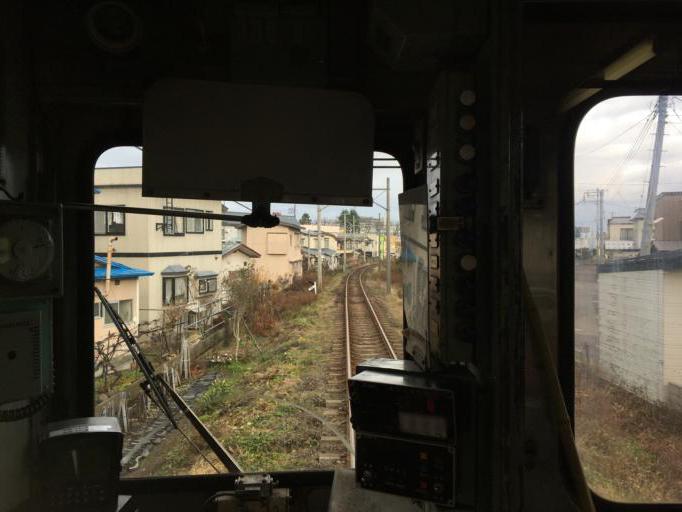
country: JP
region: Aomori
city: Hirosaki
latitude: 40.5908
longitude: 140.4684
